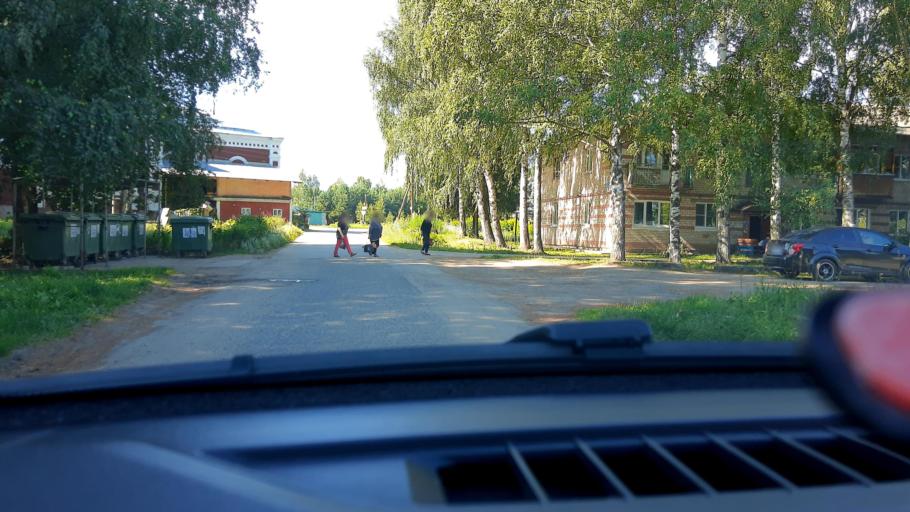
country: RU
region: Nizjnij Novgorod
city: Neklyudovo
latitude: 56.5407
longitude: 43.8292
